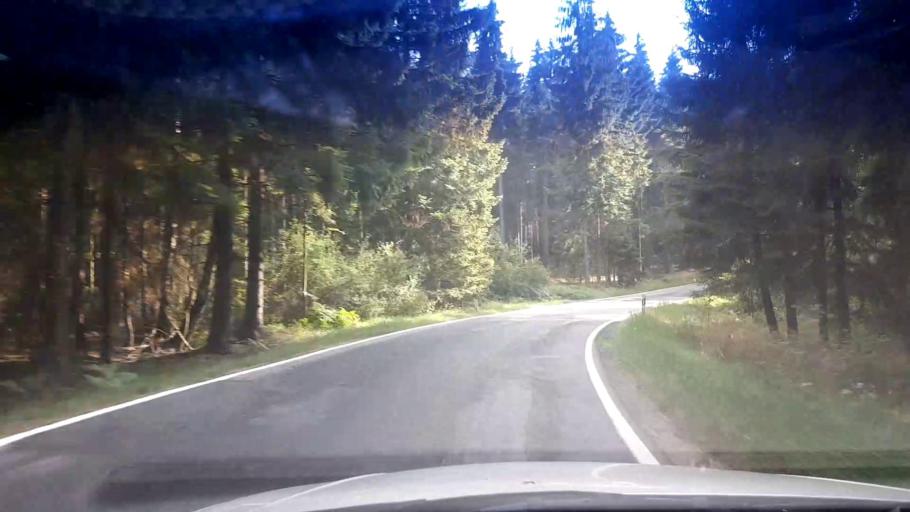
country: DE
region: Bavaria
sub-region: Upper Palatinate
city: Neualbenreuth
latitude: 49.9531
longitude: 12.4214
